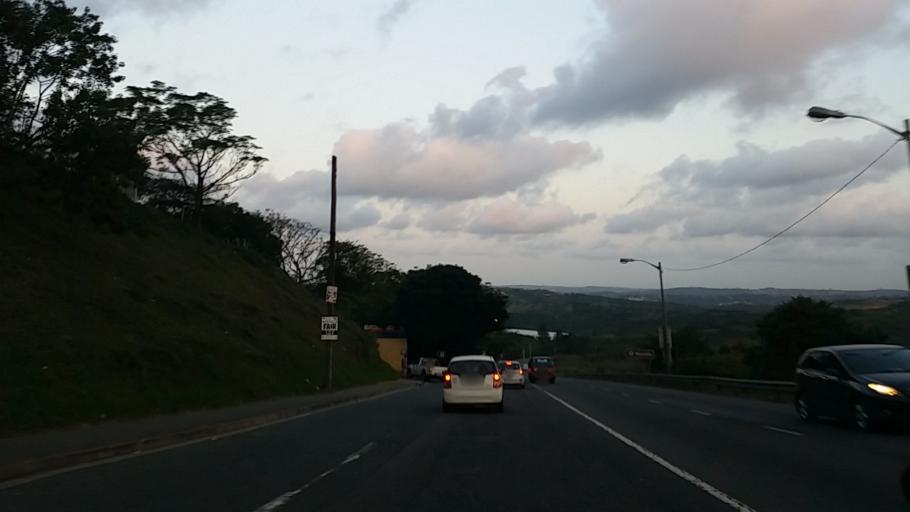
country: ZA
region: KwaZulu-Natal
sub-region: eThekwini Metropolitan Municipality
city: Berea
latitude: -29.8524
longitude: 30.9323
